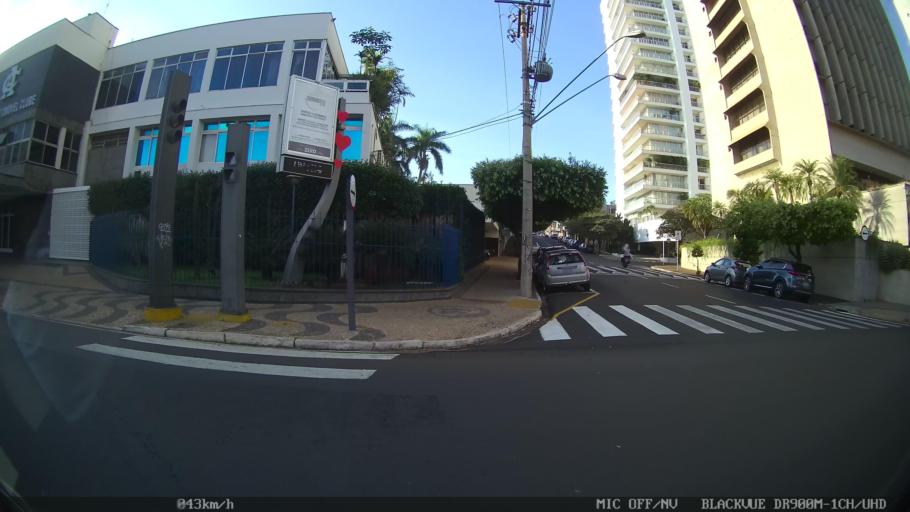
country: BR
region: Sao Paulo
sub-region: Sao Jose Do Rio Preto
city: Sao Jose do Rio Preto
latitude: -20.8130
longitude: -49.3766
